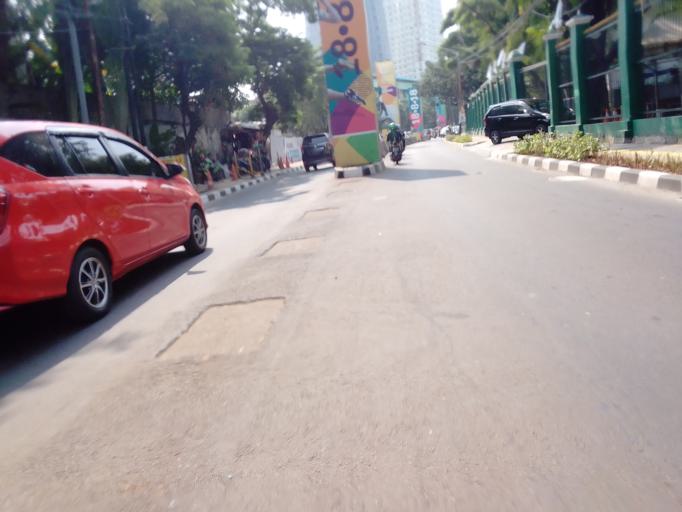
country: ID
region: Jakarta Raya
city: Jakarta
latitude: -6.2121
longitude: 106.7971
